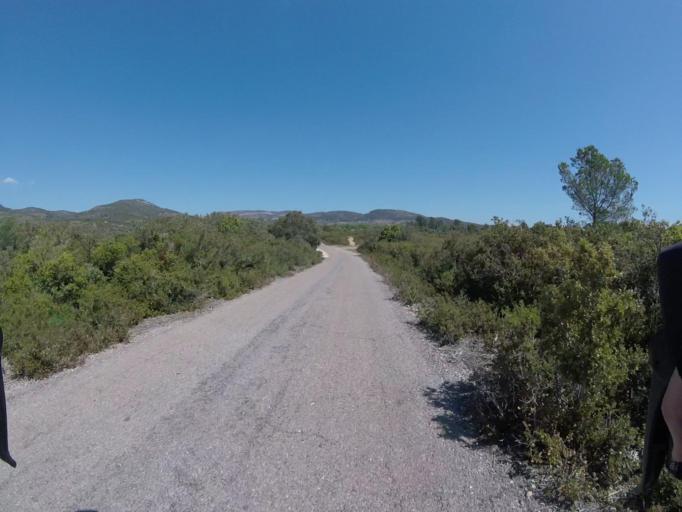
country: ES
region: Valencia
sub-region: Provincia de Castello
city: Sierra-Engarceran
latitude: 40.2392
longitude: -0.0268
